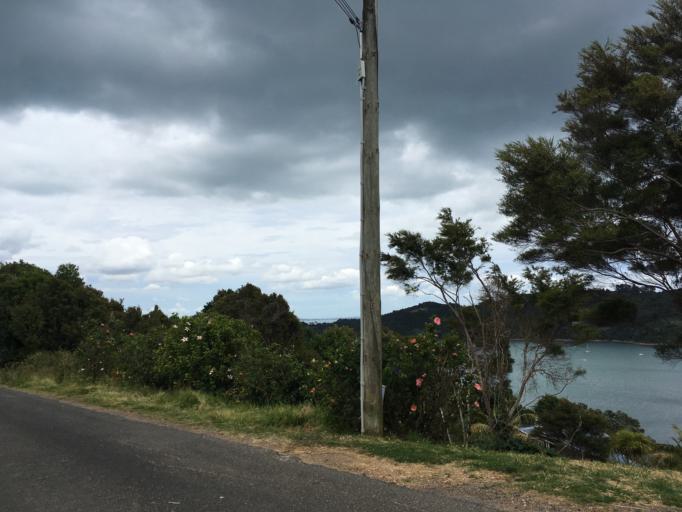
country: NZ
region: Auckland
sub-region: Auckland
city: Pakuranga
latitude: -36.7911
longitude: 175.0196
